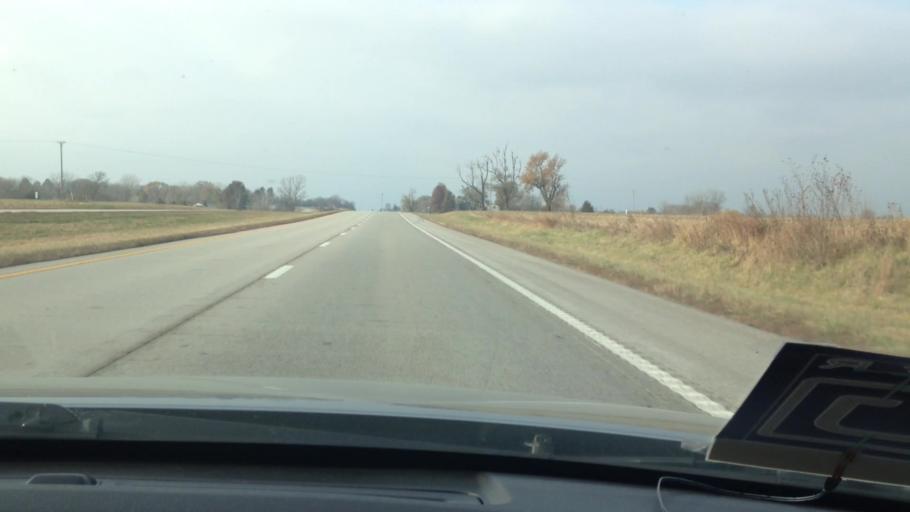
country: US
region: Missouri
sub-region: Cass County
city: Garden City
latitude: 38.5354
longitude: -94.1557
